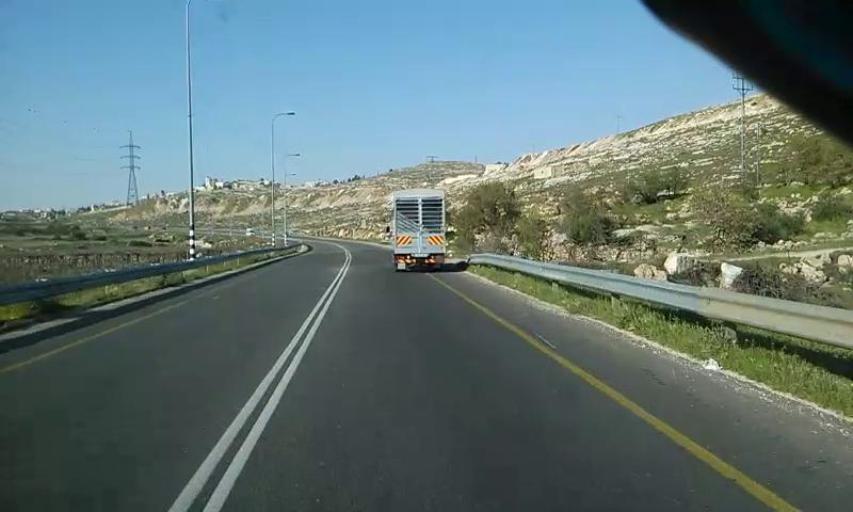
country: PS
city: Bayt `Inun
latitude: 31.5529
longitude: 35.1355
